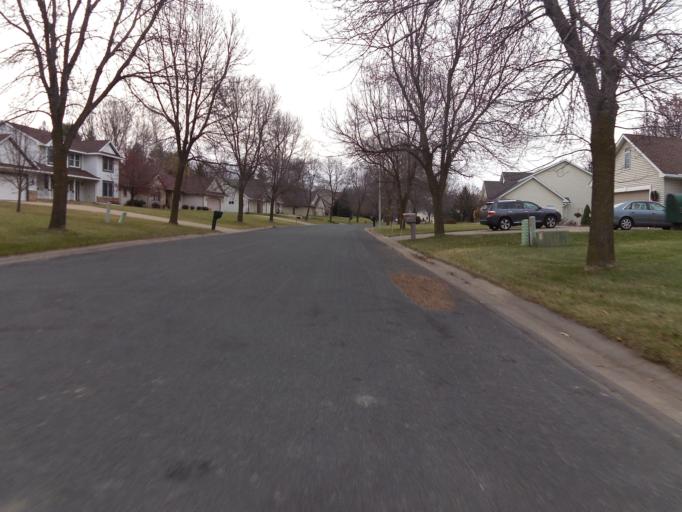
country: US
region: Wisconsin
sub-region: Pierce County
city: River Falls
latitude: 44.8607
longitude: -92.5998
